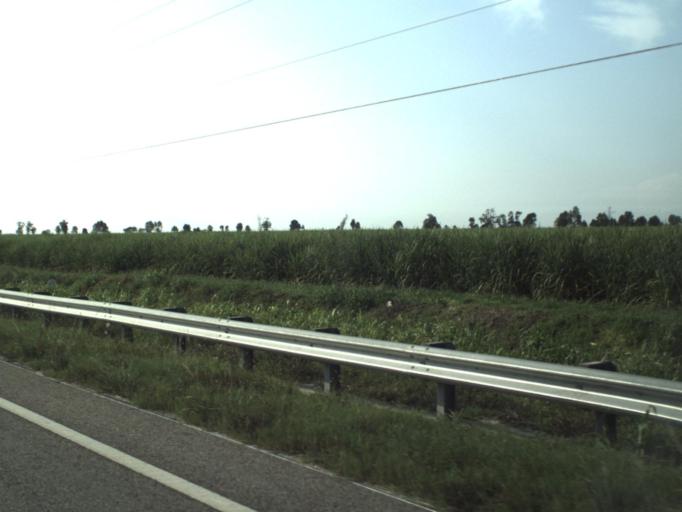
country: US
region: Florida
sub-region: Hendry County
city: Clewiston
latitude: 26.7371
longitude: -80.8720
